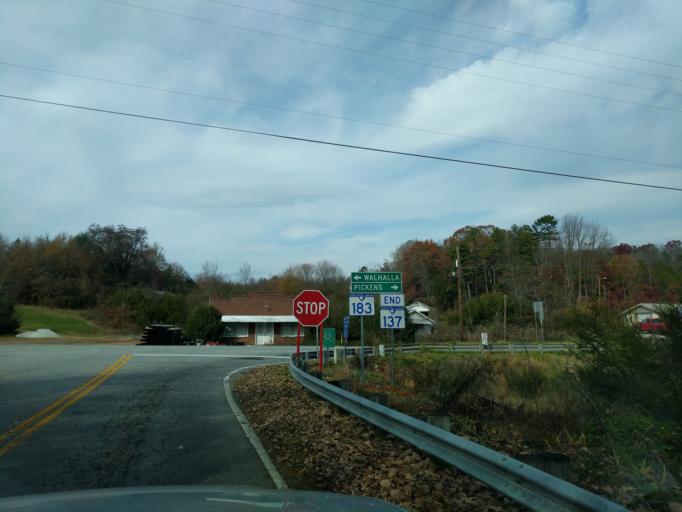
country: US
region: South Carolina
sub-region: Pickens County
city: Pickens
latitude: 34.8459
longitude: -82.8081
